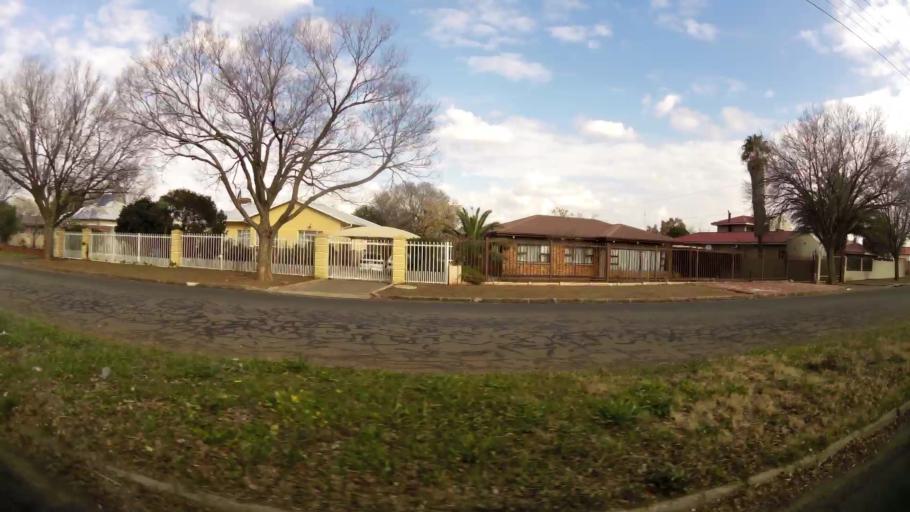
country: ZA
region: Orange Free State
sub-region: Mangaung Metropolitan Municipality
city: Bloemfontein
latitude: -29.0799
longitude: 26.2429
